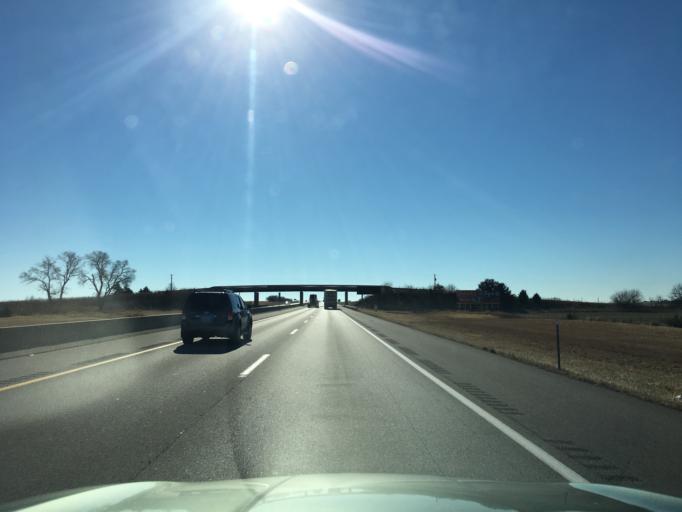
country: US
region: Kansas
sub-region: Sumner County
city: Wellington
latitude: 37.3065
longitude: -97.3405
